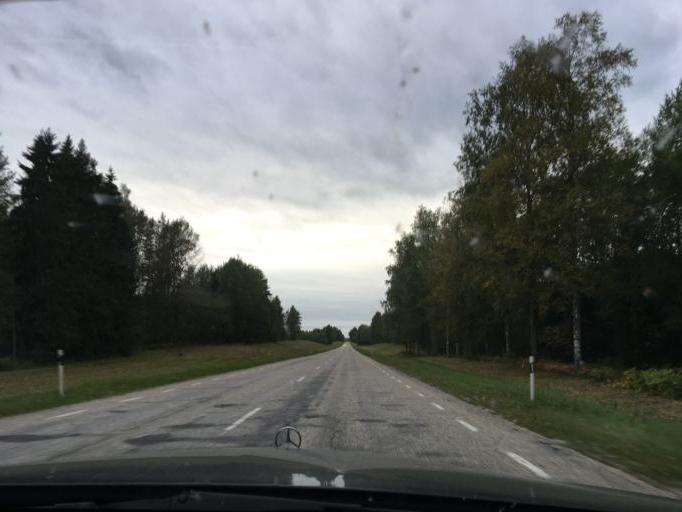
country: LV
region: Aluksnes Rajons
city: Aluksne
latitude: 57.5979
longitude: 27.1955
